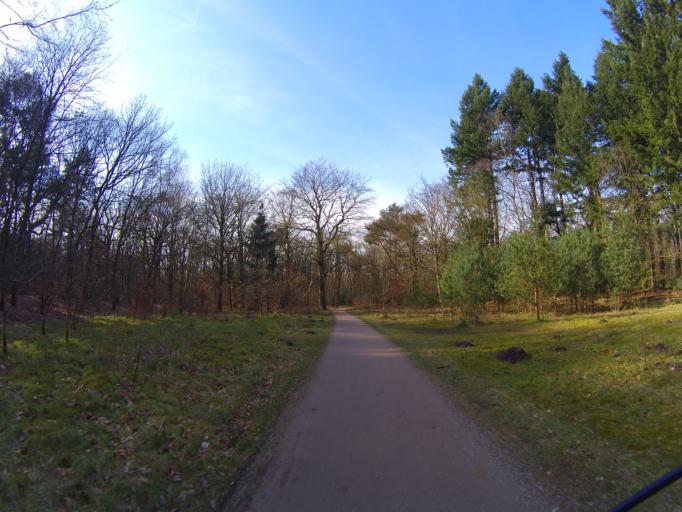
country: NL
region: North Holland
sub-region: Gemeente Bussum
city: Bussum
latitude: 52.2584
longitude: 5.1583
